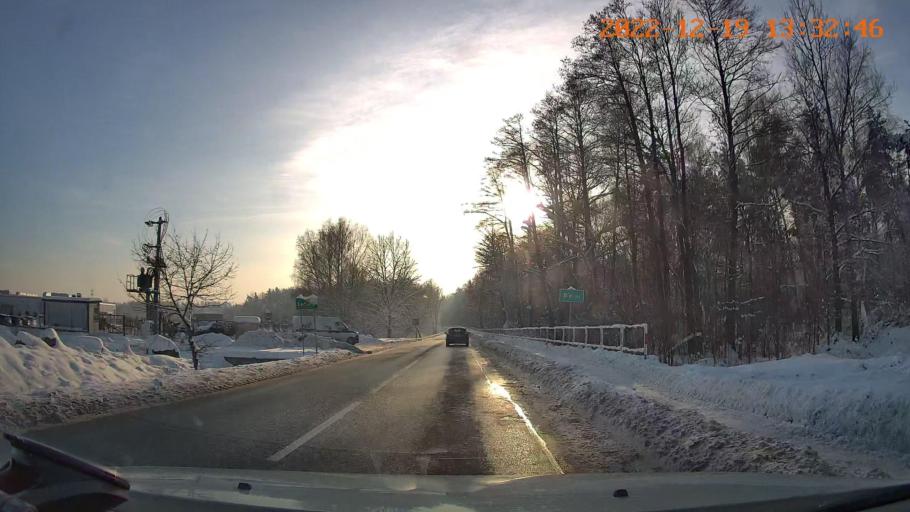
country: PL
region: Silesian Voivodeship
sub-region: Powiat bierunsko-ledzinski
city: Bierun
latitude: 50.1092
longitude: 19.0992
